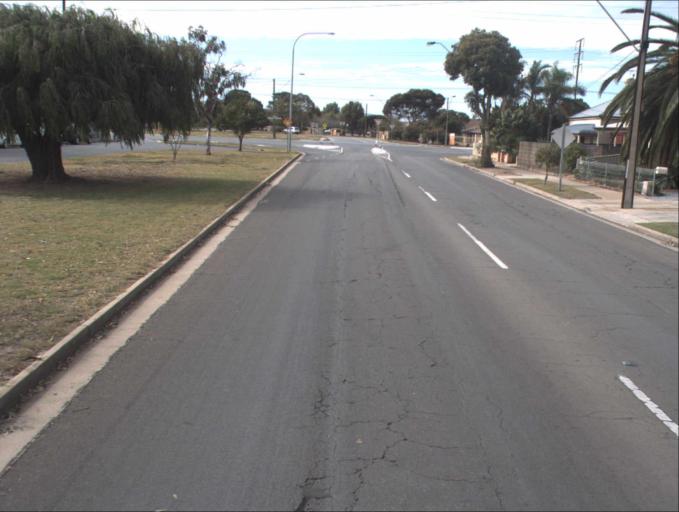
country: AU
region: South Australia
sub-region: Port Adelaide Enfield
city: Birkenhead
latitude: -34.8122
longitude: 138.5001
